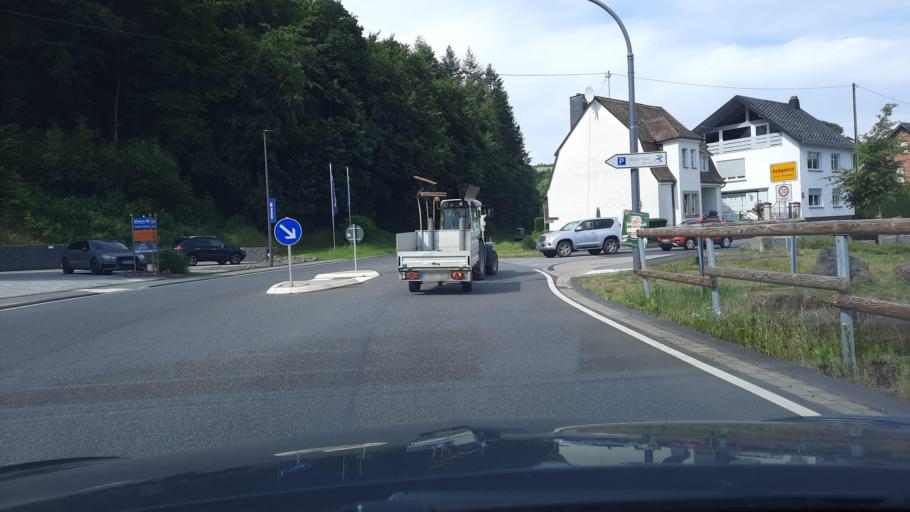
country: DE
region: Rheinland-Pfalz
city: Kempenich
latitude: 50.4174
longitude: 7.1222
